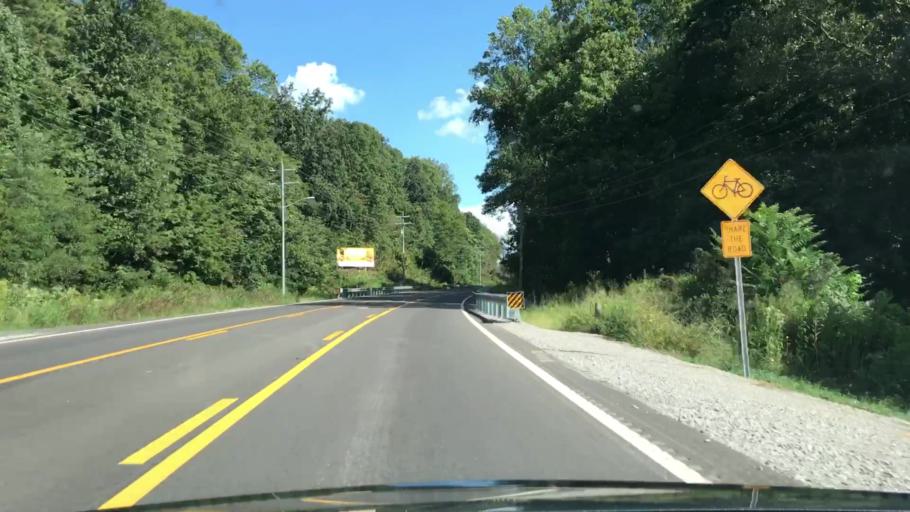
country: US
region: Alabama
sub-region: Limestone County
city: Ardmore
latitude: 35.0041
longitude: -86.8705
